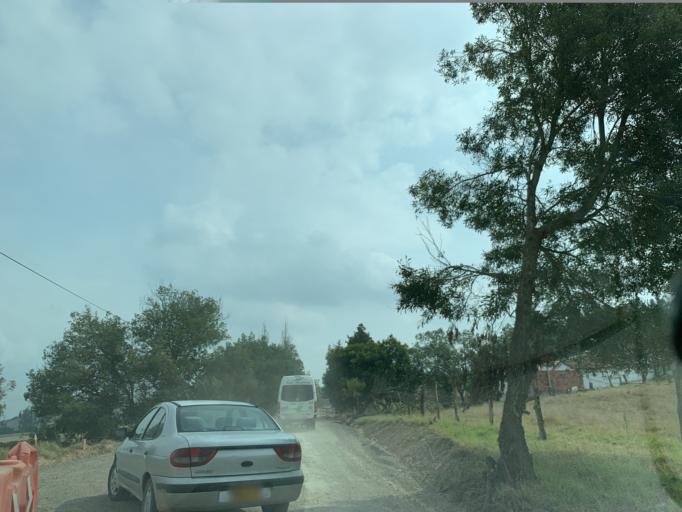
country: CO
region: Boyaca
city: Tunja
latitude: 5.5364
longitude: -73.3060
